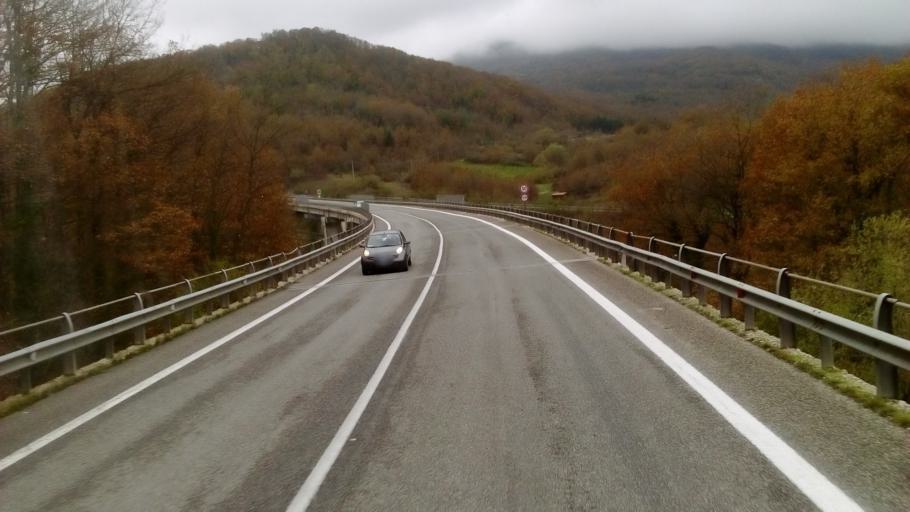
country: IT
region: Molise
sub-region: Provincia di Isernia
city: Pescolanciano
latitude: 41.6719
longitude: 14.3520
